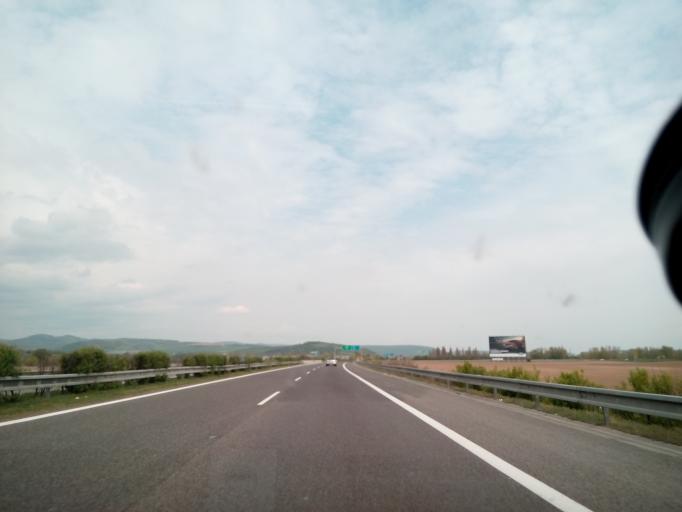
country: SK
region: Trenciansky
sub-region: Okres Trencin
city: Trencin
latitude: 48.8530
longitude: 17.9506
